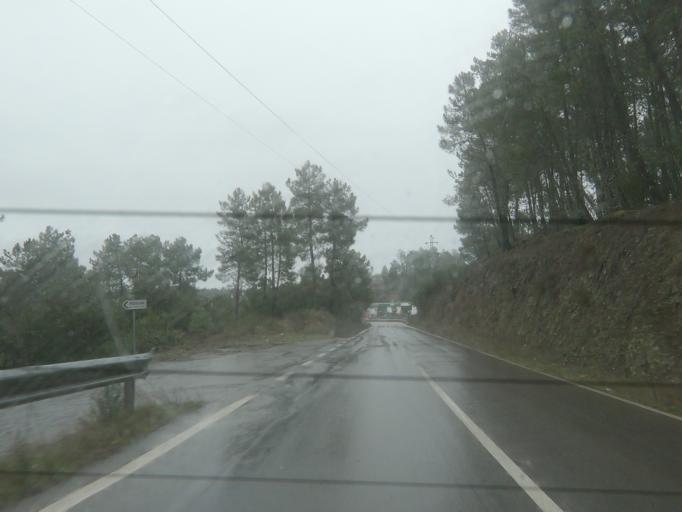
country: PT
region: Vila Real
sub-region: Sabrosa
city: Vilela
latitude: 41.2333
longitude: -7.6822
